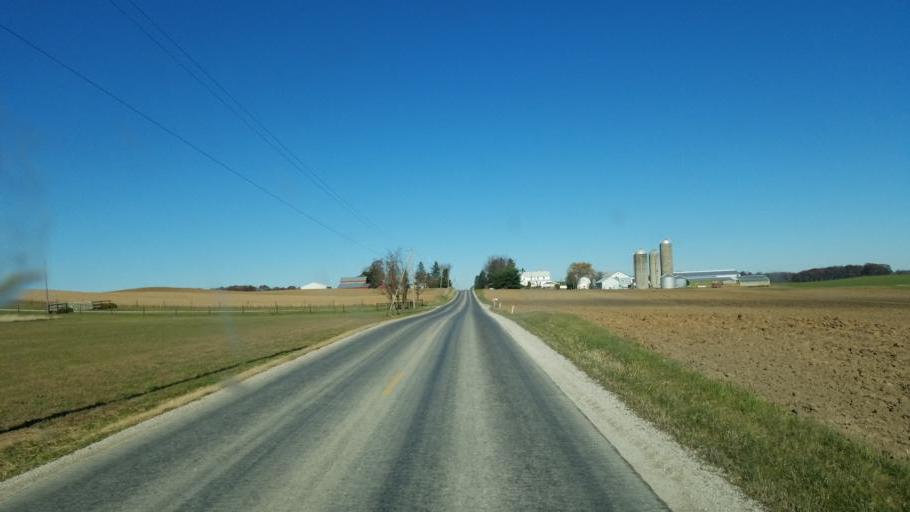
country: US
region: Ohio
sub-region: Huron County
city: Plymouth
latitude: 40.9469
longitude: -82.6194
